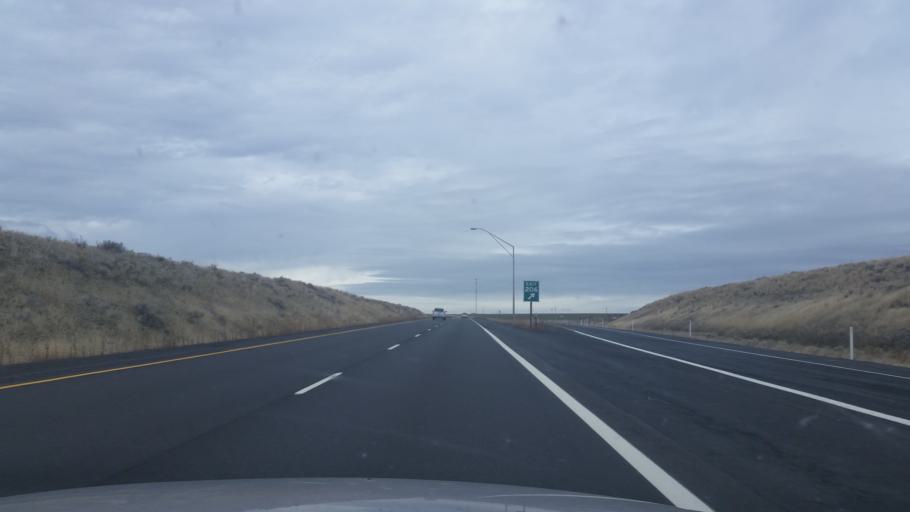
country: US
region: Washington
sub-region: Adams County
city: Ritzville
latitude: 47.0972
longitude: -118.6621
